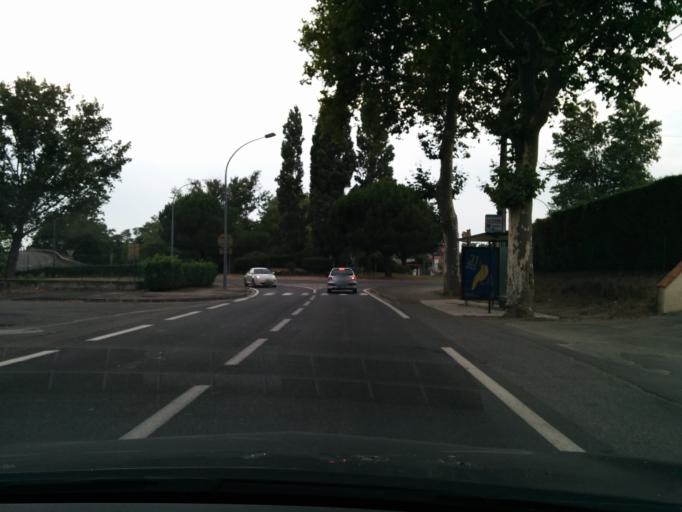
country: FR
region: Midi-Pyrenees
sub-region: Departement de la Haute-Garonne
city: Villefranche-de-Lauragais
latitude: 43.4054
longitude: 1.7098
